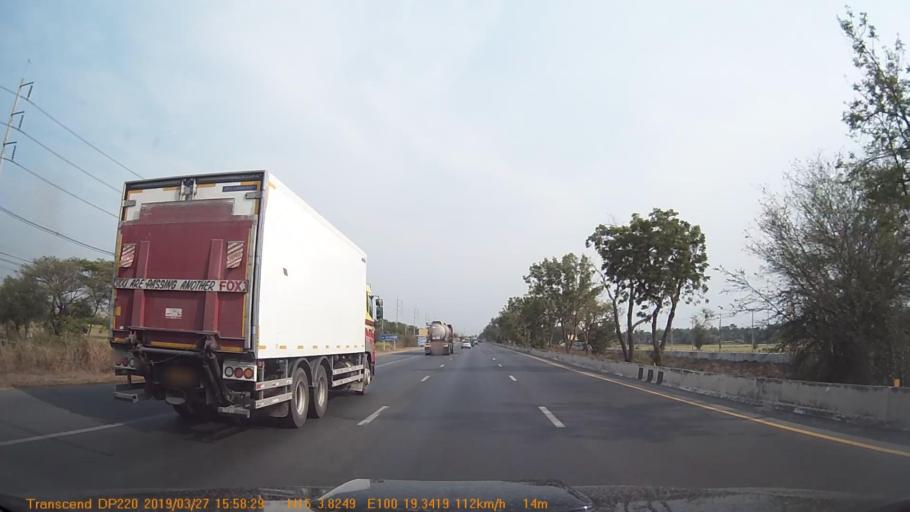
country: TH
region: Sing Buri
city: In Buri
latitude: 15.0634
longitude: 100.3225
